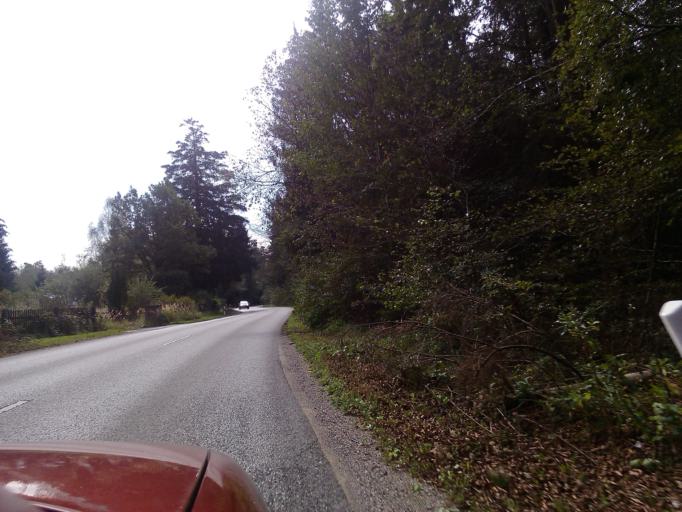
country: DE
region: Bavaria
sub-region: Upper Bavaria
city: Gauting
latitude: 48.0825
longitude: 11.3758
